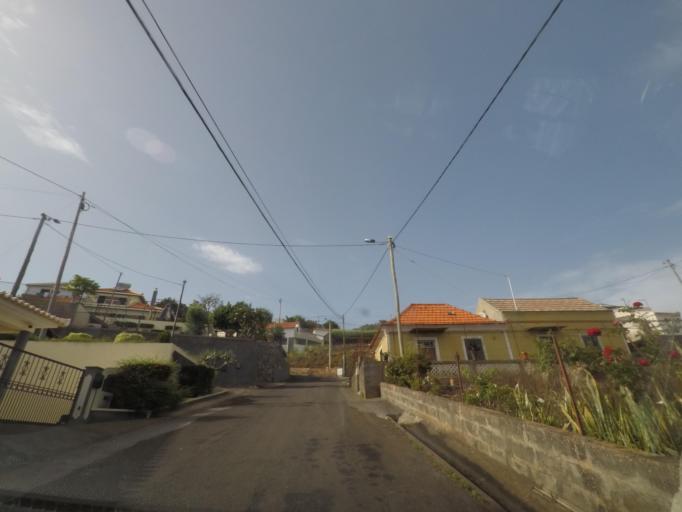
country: PT
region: Madeira
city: Ponta do Sol
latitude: 32.6953
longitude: -17.1165
